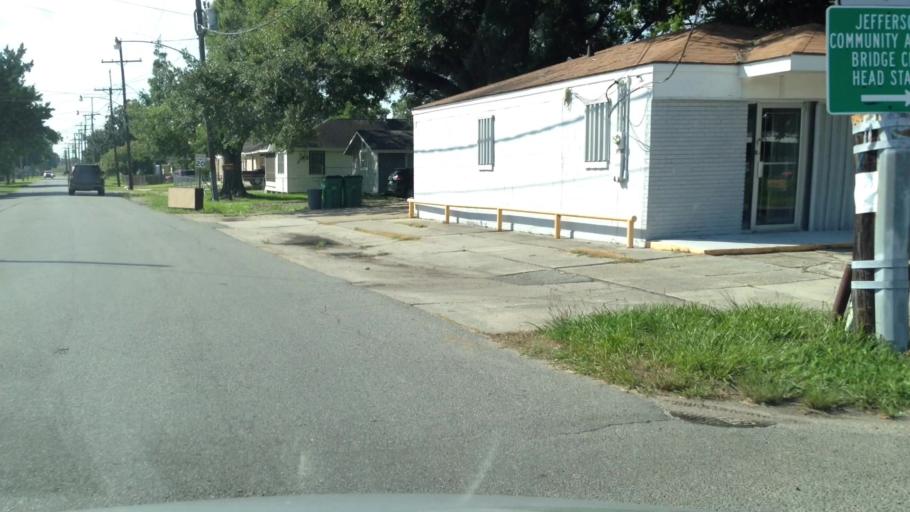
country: US
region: Louisiana
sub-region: Jefferson Parish
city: Bridge City
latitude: 29.9304
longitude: -90.1673
